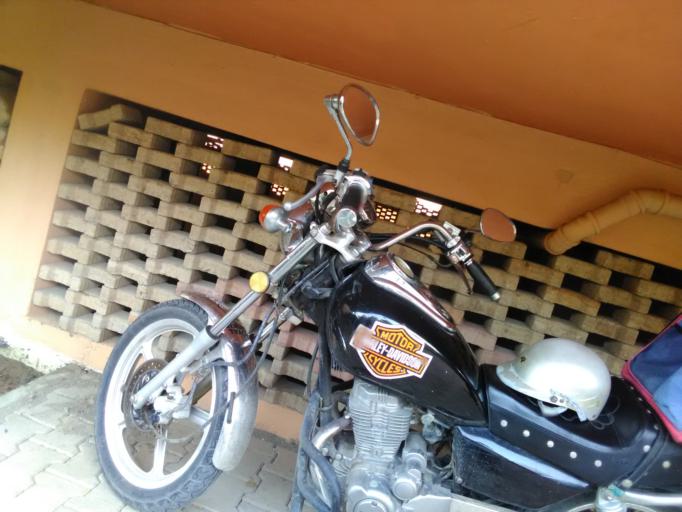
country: TR
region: Antalya
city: Gazipasa
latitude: 36.2637
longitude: 32.2870
